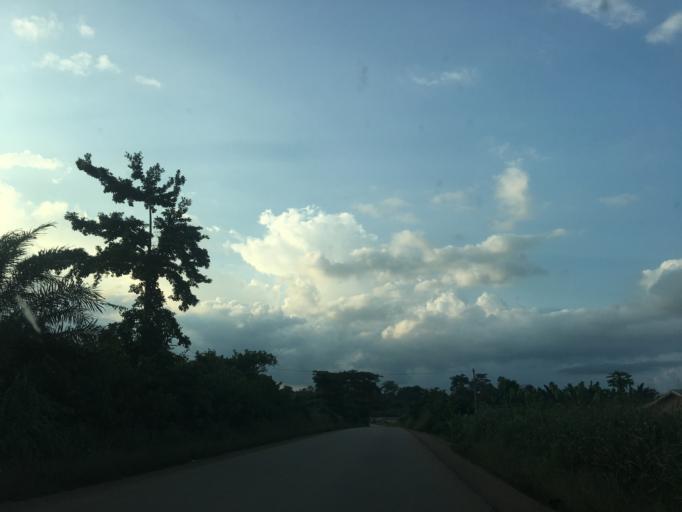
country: GH
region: Western
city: Bibiani
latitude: 6.6573
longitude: -2.4264
